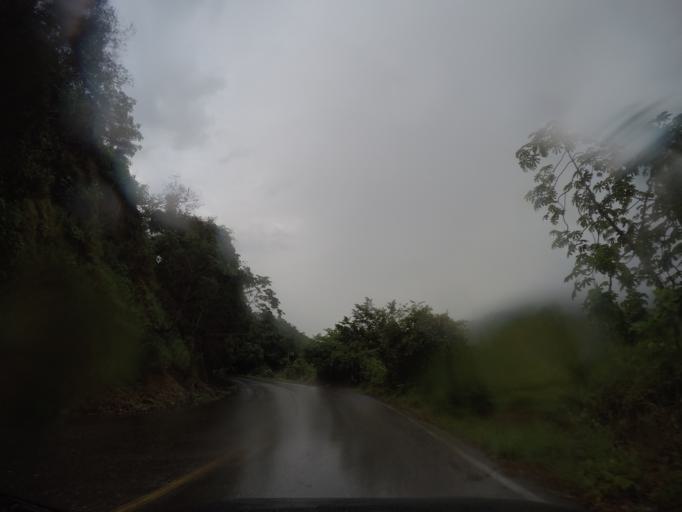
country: MX
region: Oaxaca
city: San Gabriel Mixtepec
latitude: 16.0690
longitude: -97.0763
